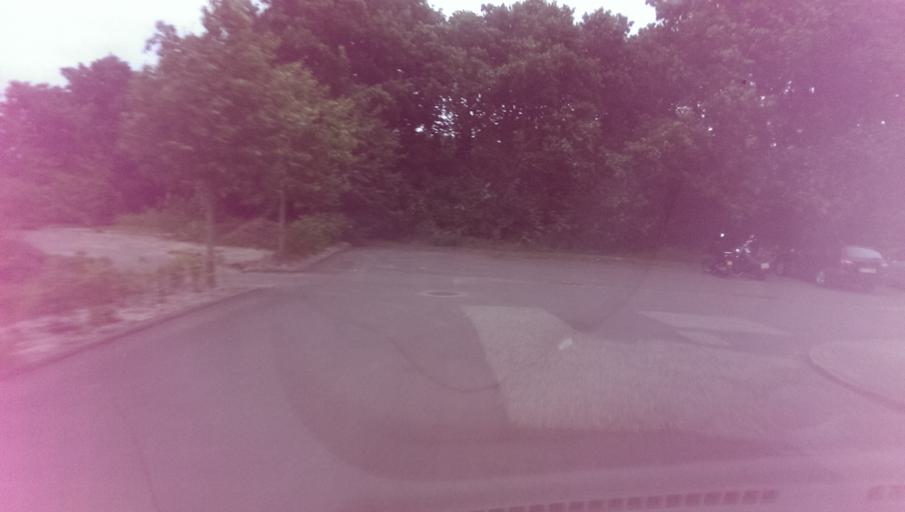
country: DK
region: South Denmark
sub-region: Esbjerg Kommune
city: Esbjerg
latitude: 55.4737
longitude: 8.4904
